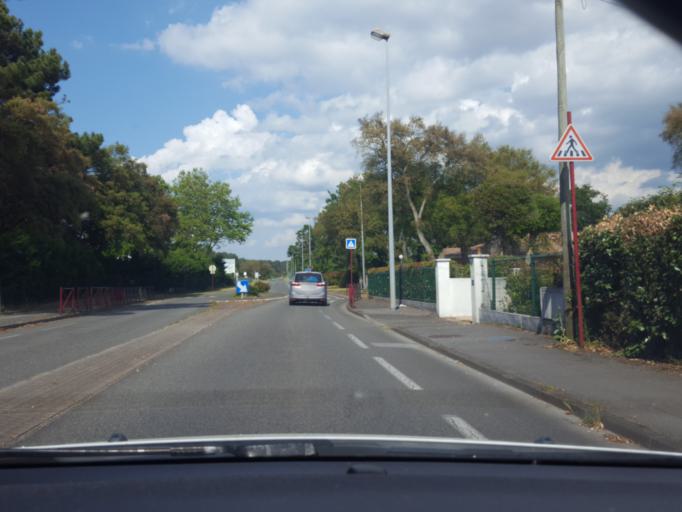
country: FR
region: Aquitaine
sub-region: Departement des Landes
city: Tarnos
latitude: 43.5485
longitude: -1.4858
